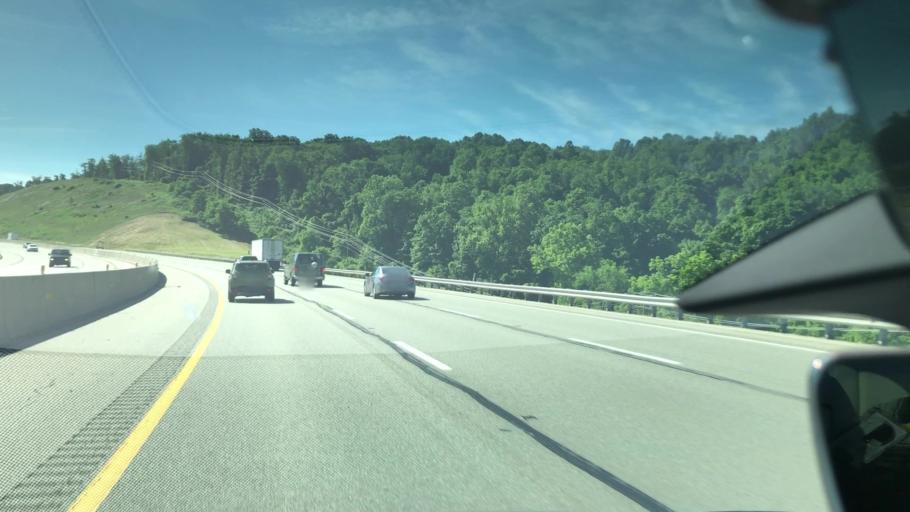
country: US
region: Pennsylvania
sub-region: Westmoreland County
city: Irwin
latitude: 40.2668
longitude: -79.6671
